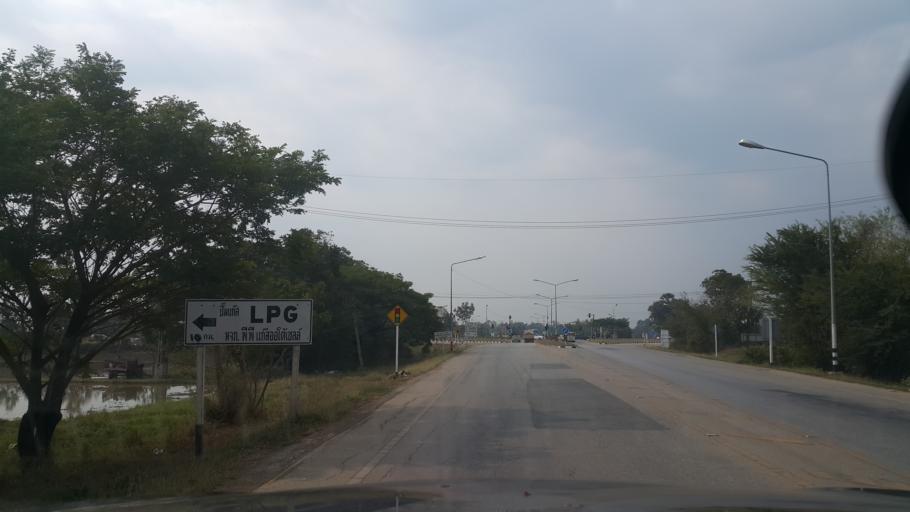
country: TH
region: Sukhothai
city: Sukhothai
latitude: 17.0658
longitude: 99.8773
